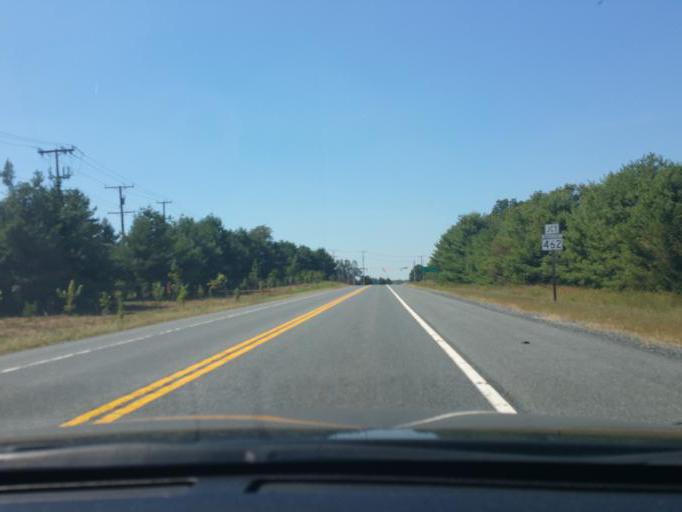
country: US
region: Maryland
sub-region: Harford County
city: Aberdeen
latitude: 39.5730
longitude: -76.1663
